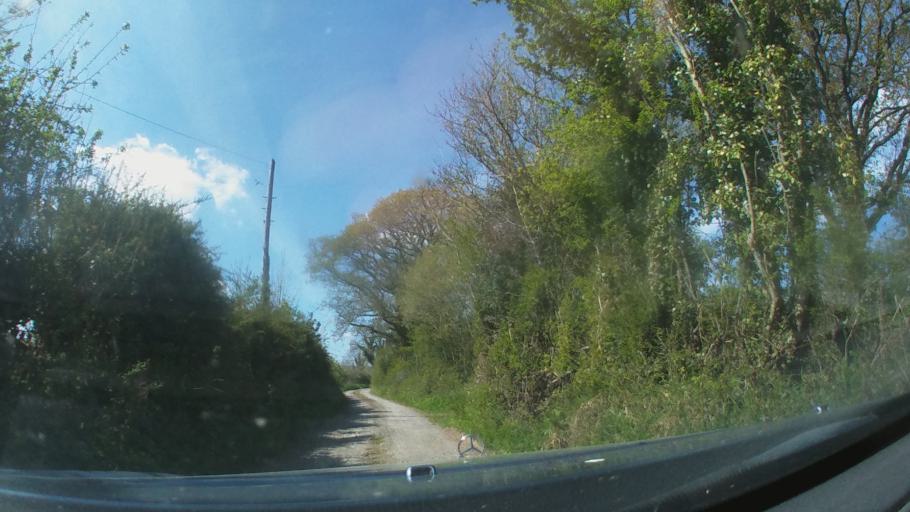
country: IE
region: Leinster
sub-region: Kilkenny
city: Callan
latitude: 52.6005
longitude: -7.3903
